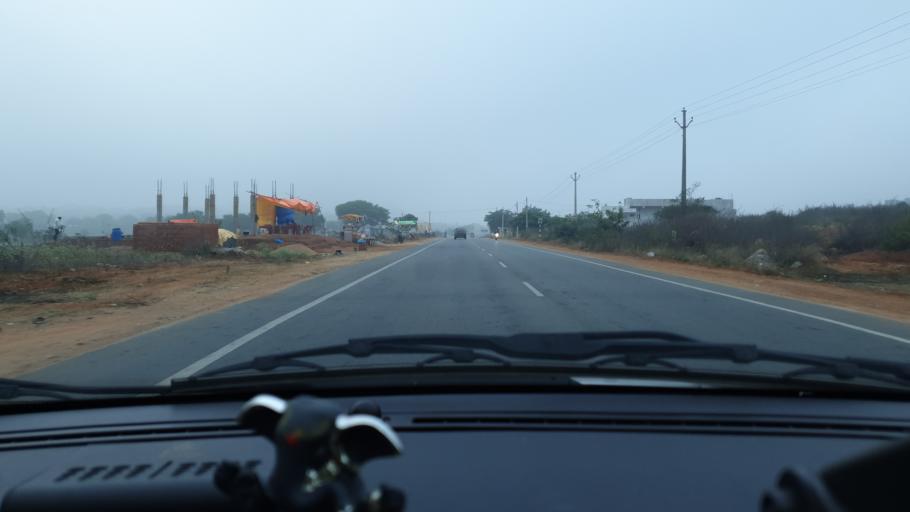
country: IN
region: Telangana
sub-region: Mahbubnagar
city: Farrukhnagar
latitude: 16.9399
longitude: 78.5271
